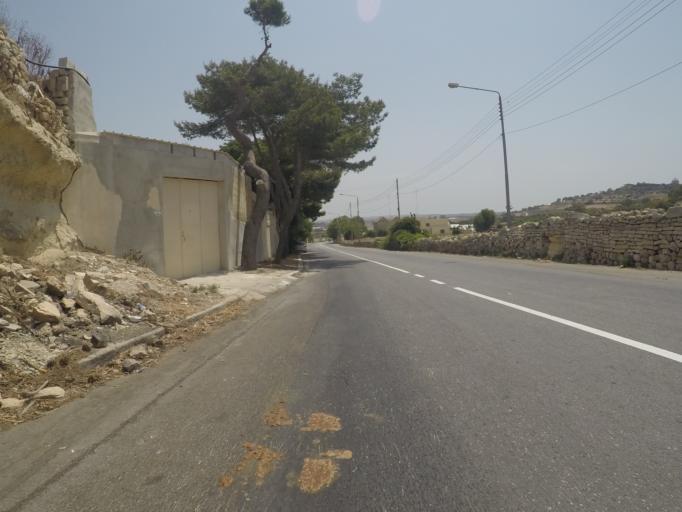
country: MT
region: L-Imdina
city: Imdina
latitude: 35.8825
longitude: 14.4058
